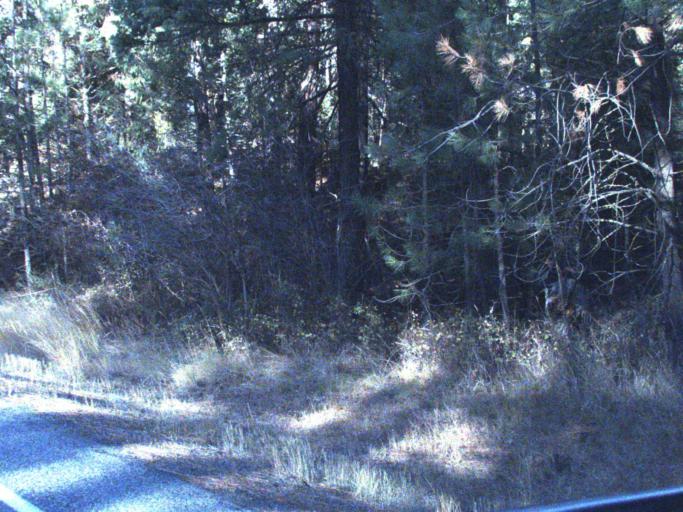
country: US
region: Washington
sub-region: Ferry County
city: Republic
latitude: 48.6506
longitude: -118.6778
